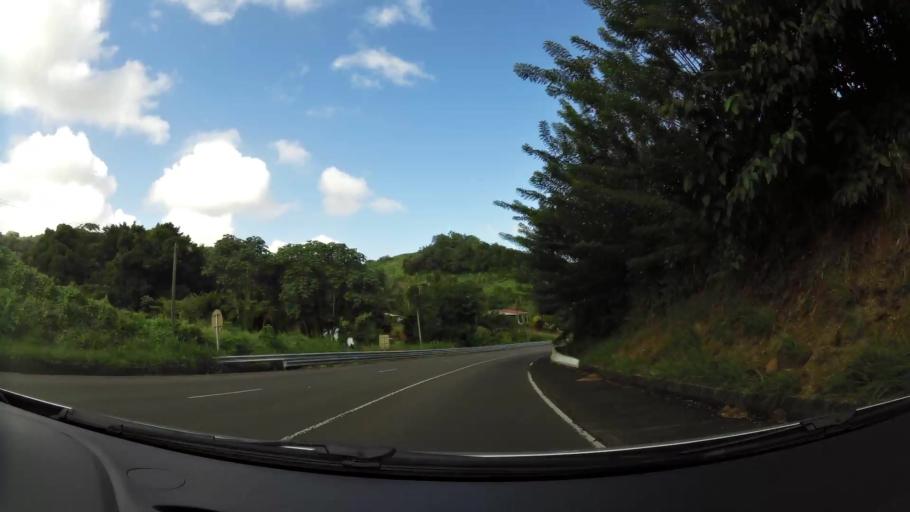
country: MQ
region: Martinique
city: Petite Riviere Salee
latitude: 14.7533
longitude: -60.9779
